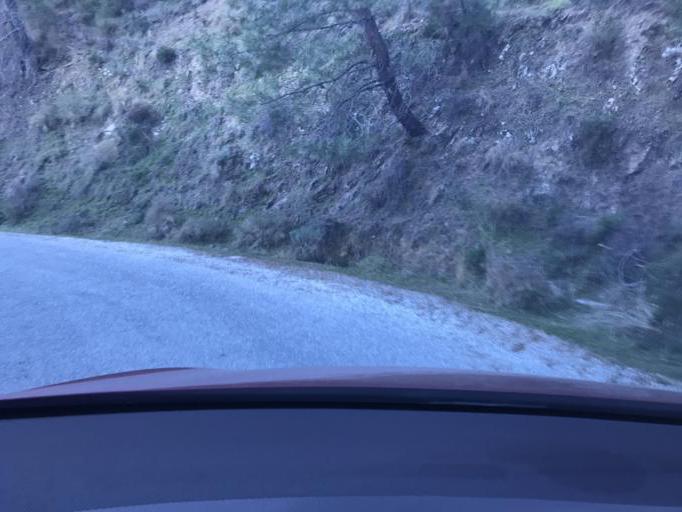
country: ES
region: Andalusia
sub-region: Provincia de Malaga
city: Tolox
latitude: 36.6827
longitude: -4.9191
